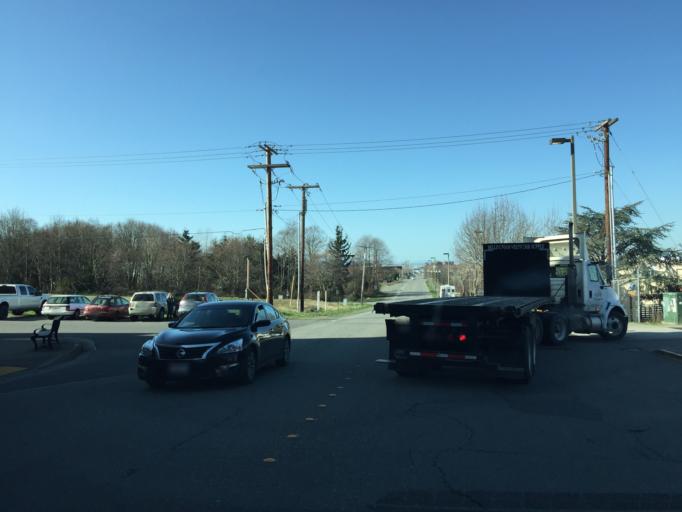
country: US
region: Washington
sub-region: Whatcom County
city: Bellingham
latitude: 48.7202
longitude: -122.5053
